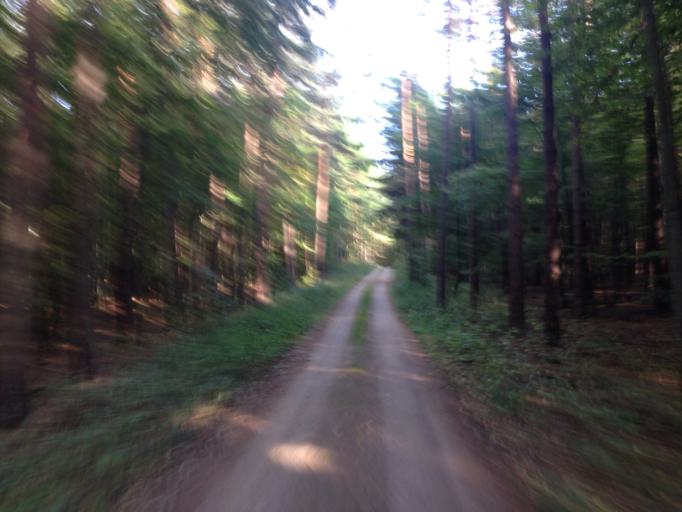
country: PL
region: Warmian-Masurian Voivodeship
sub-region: Powiat dzialdowski
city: Lidzbark
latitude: 53.2448
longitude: 19.7395
